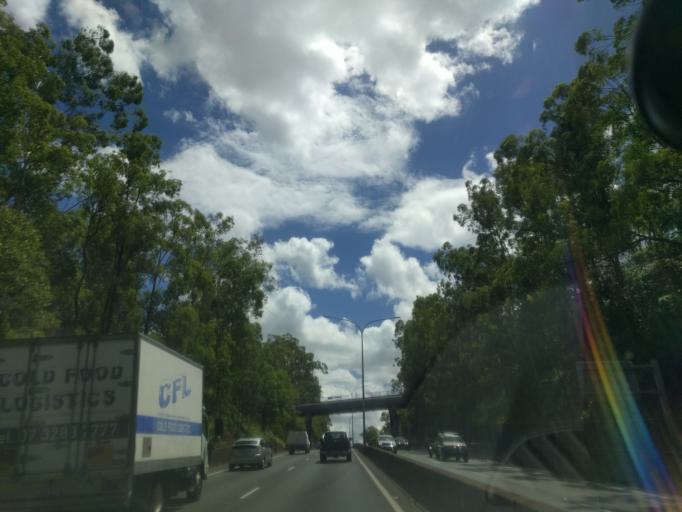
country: AU
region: Queensland
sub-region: Brisbane
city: Kenmore Hills
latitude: -27.5255
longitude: 152.9473
